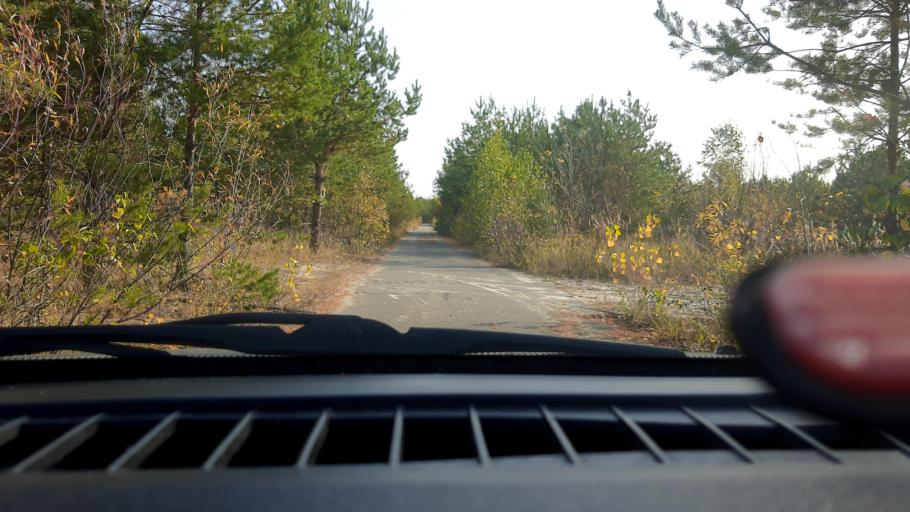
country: RU
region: Nizjnij Novgorod
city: Gorbatovka
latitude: 56.3564
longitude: 43.7631
